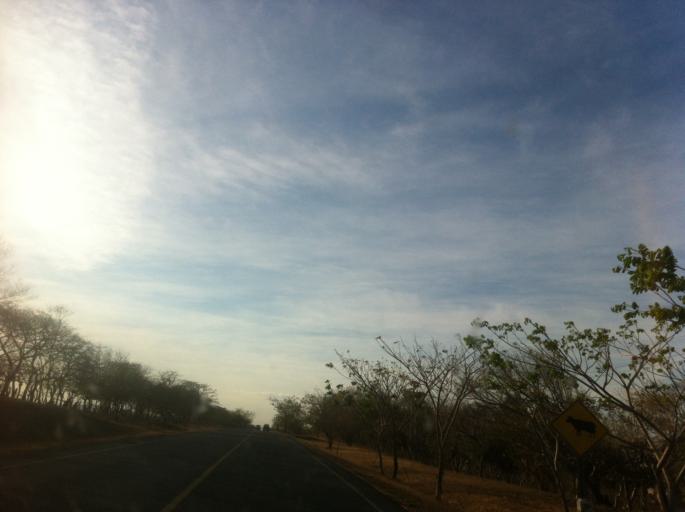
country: NI
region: Rivas
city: Rivas
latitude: 11.3839
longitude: -85.7646
